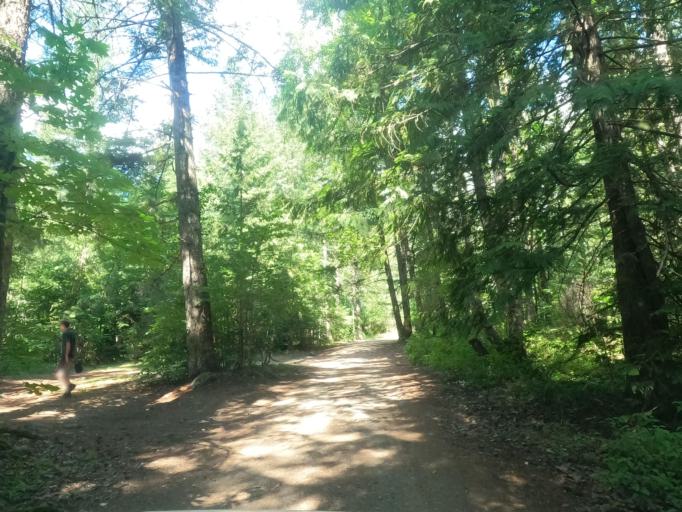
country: CA
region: British Columbia
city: Pemberton
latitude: 50.3498
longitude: -122.7298
